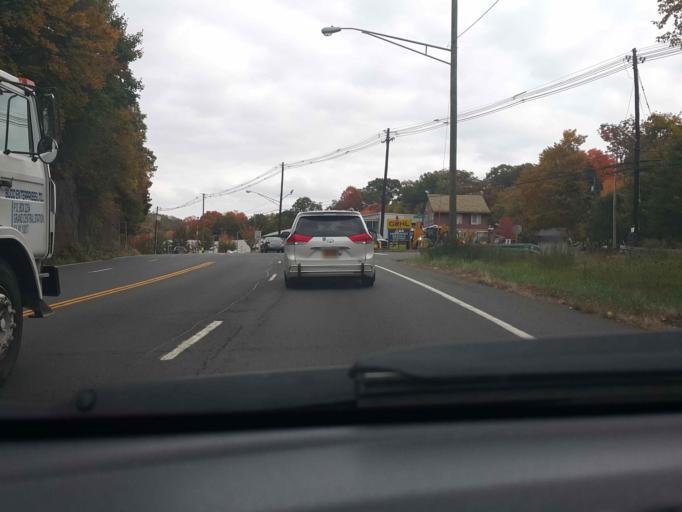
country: US
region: New York
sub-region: Rockland County
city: South Nyack
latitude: 41.0928
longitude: -73.9433
